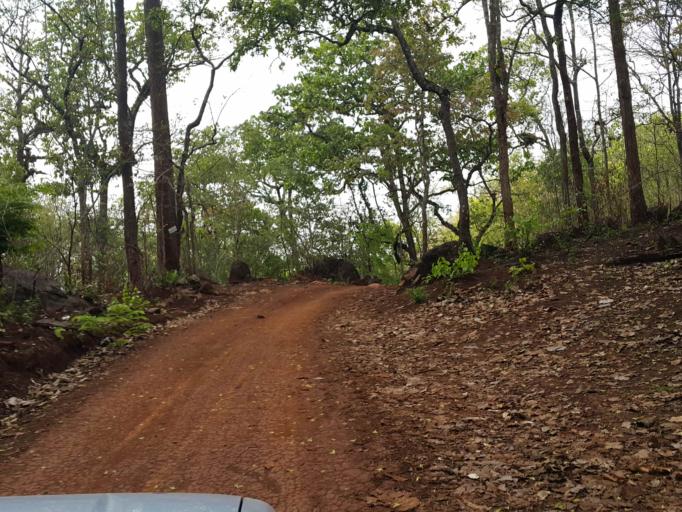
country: TH
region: Chiang Mai
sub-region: Amphoe Chiang Dao
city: Chiang Dao
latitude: 19.3054
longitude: 98.7261
